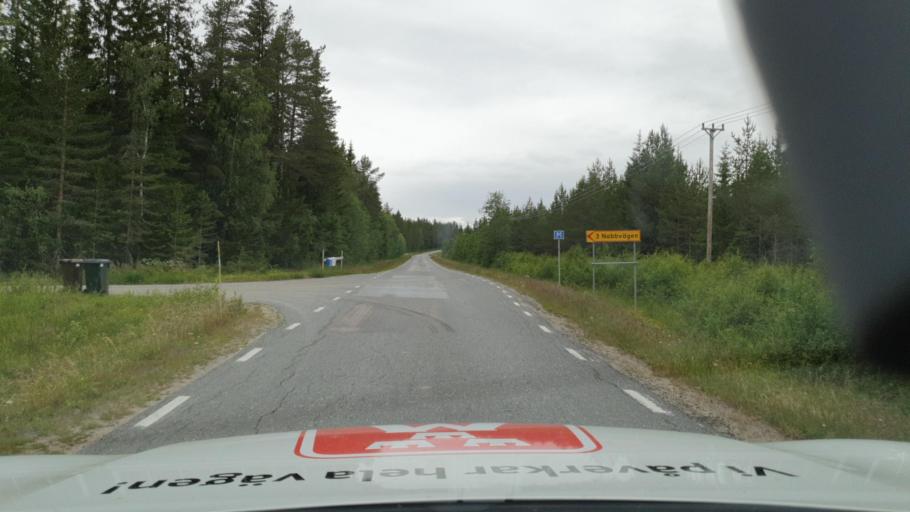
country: SE
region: Vaesterbotten
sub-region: Nordmalings Kommun
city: Nordmaling
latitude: 63.4847
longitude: 19.4462
